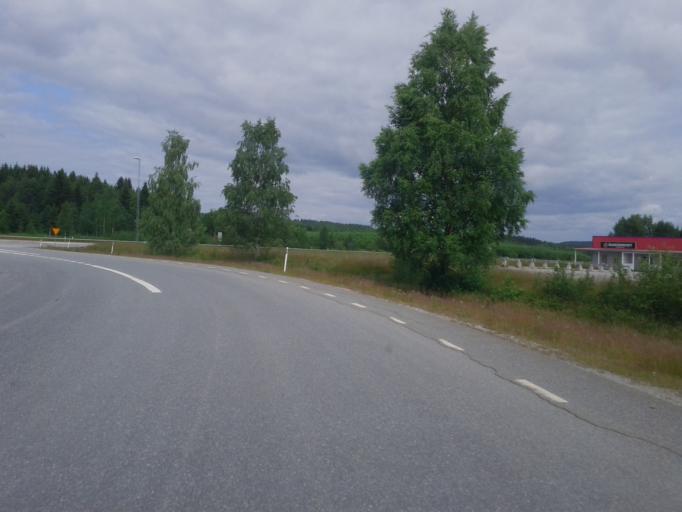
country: SE
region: Vaesternorrland
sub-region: OErnskoeldsviks Kommun
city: Bjasta
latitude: 63.2071
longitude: 18.4894
